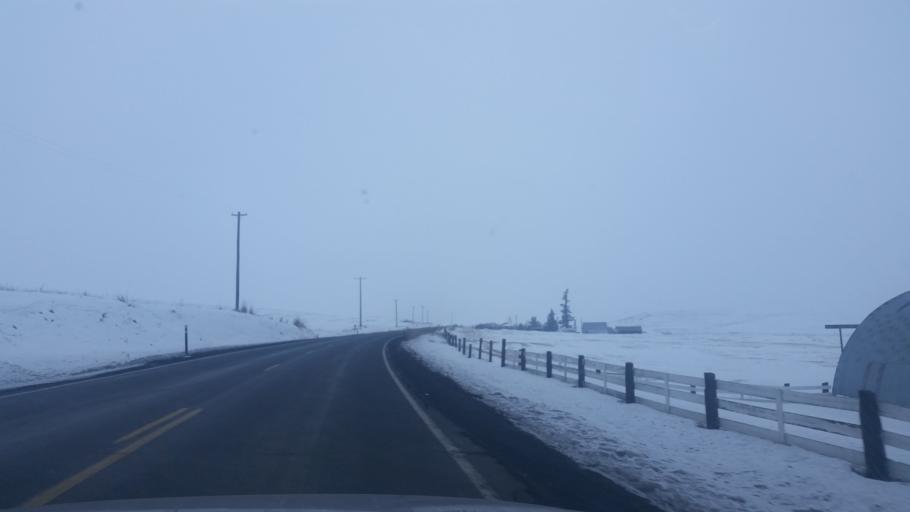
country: US
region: Washington
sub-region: Spokane County
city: Medical Lake
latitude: 47.7133
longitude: -117.8722
